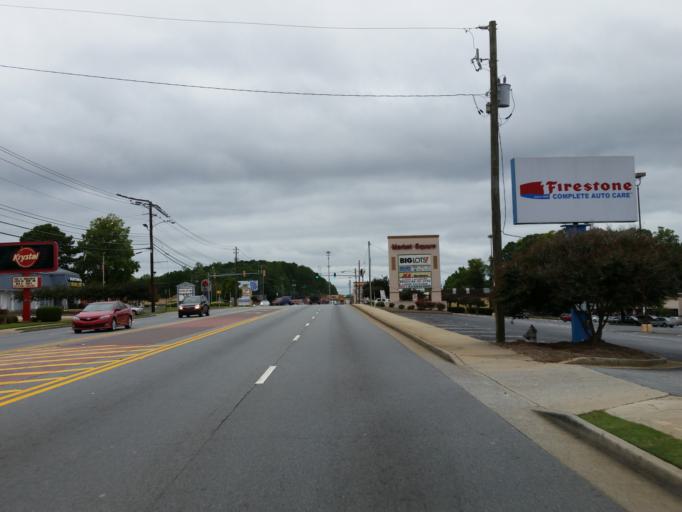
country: US
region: Georgia
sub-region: Cobb County
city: Marietta
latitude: 34.0218
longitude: -84.5285
